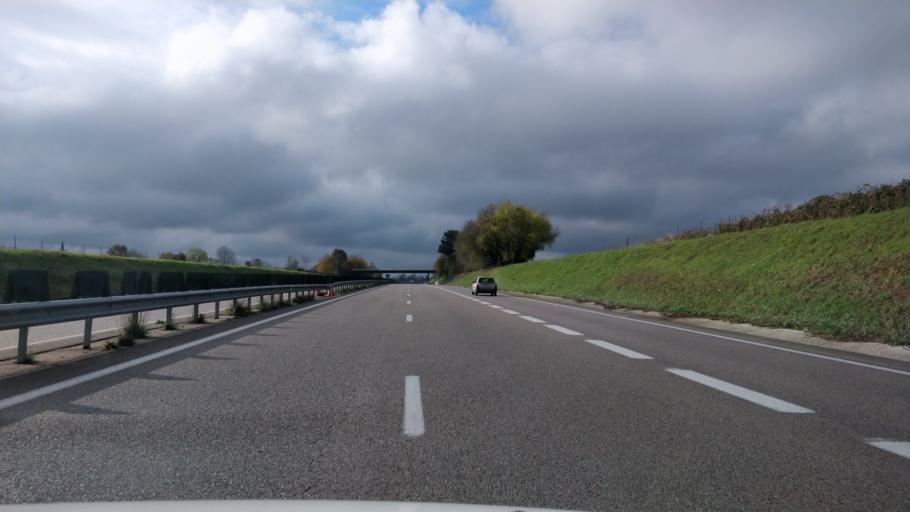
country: FR
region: Haute-Normandie
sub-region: Departement de l'Eure
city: Toutainville
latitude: 49.3382
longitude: 0.4163
